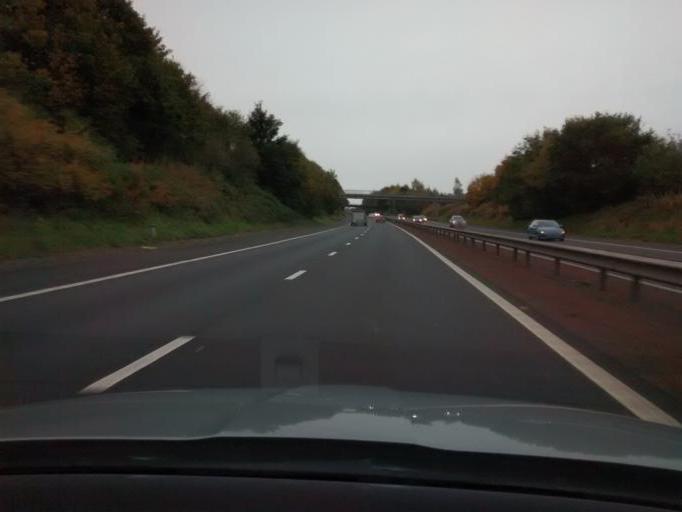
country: GB
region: Scotland
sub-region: Stirling
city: Stirling
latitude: 56.1139
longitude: -3.9658
